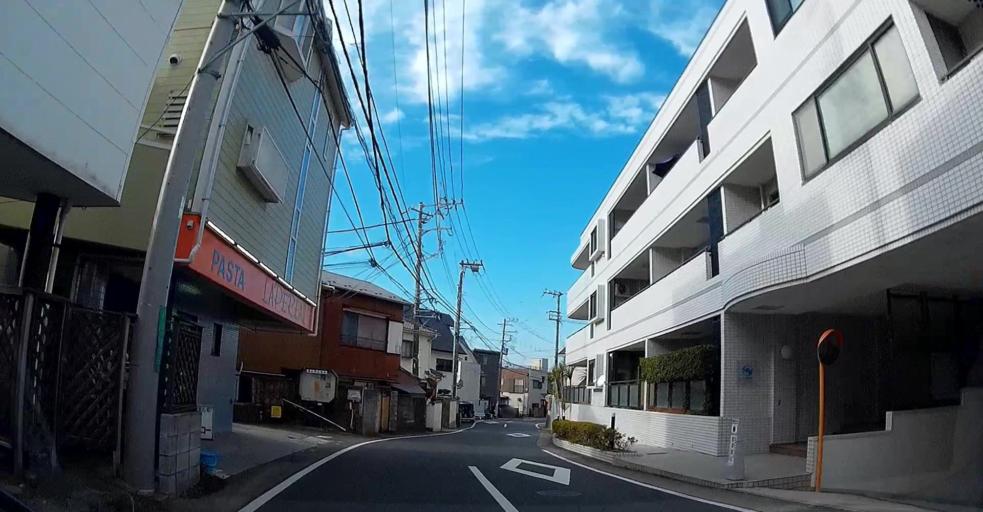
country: JP
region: Kanagawa
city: Hayama
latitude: 35.2788
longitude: 139.5716
